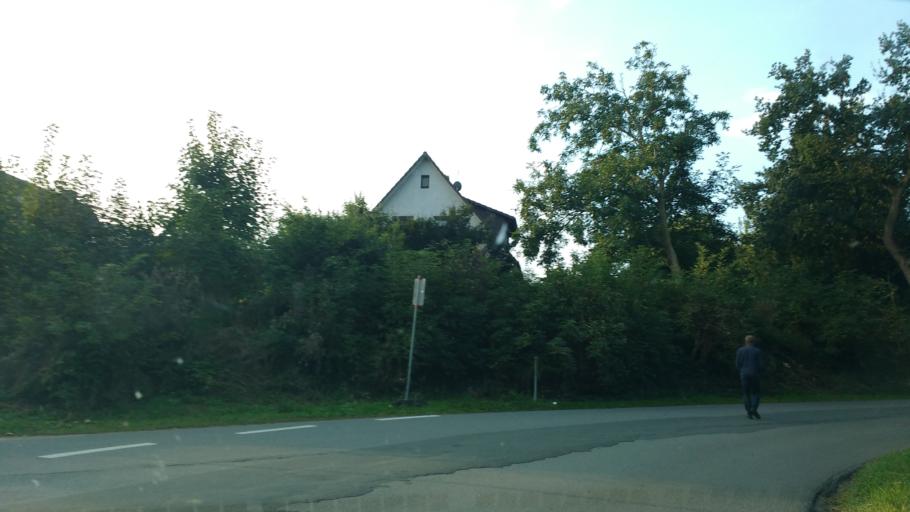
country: DE
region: Lower Saxony
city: Bad Pyrmont
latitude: 51.9807
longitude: 9.2834
